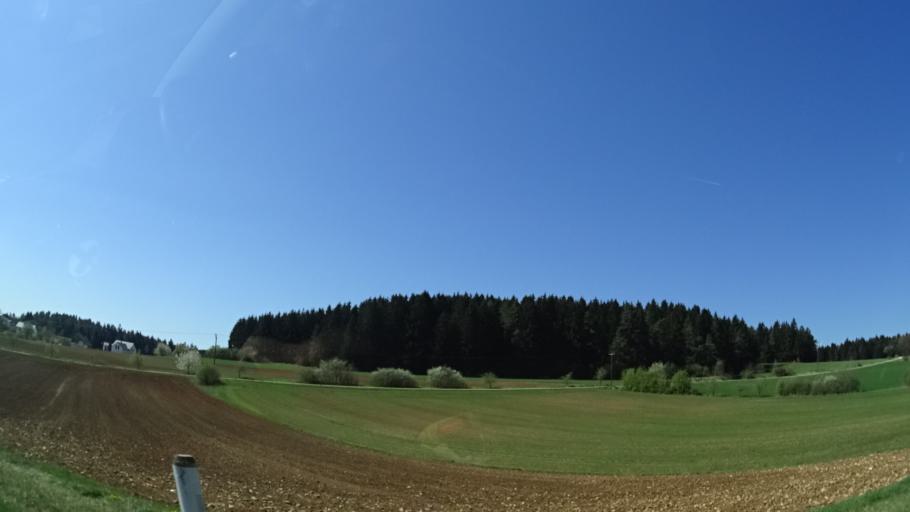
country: DE
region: Bavaria
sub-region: Upper Palatinate
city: Lauterhofen
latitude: 49.4087
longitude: 11.6160
